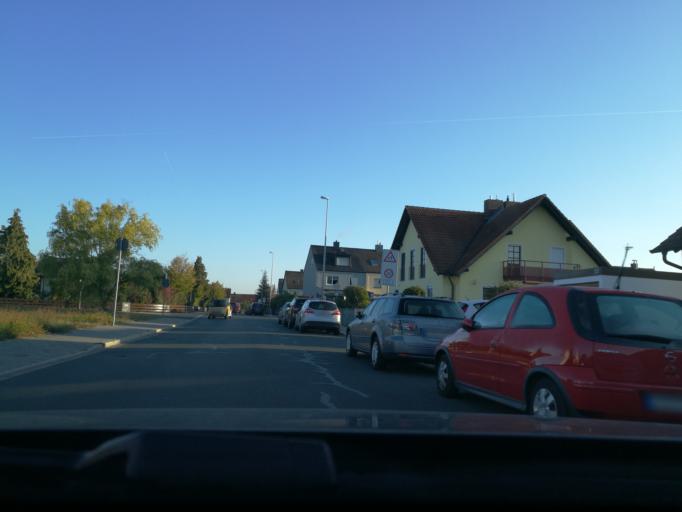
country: DE
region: Bavaria
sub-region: Regierungsbezirk Mittelfranken
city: Herzogenaurach
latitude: 49.5608
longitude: 10.8807
